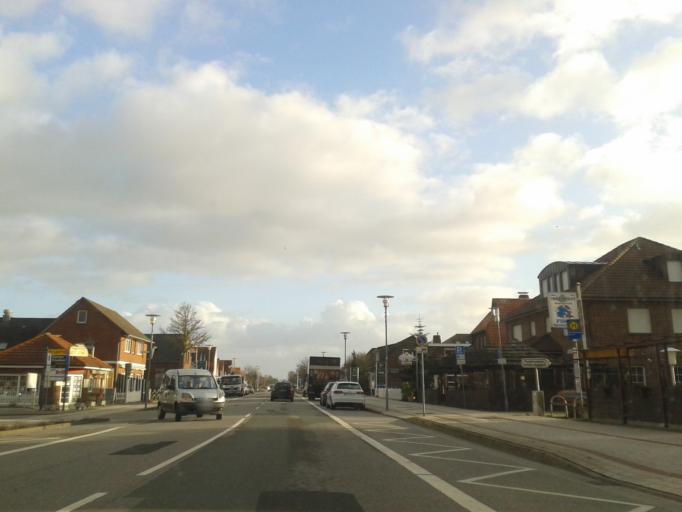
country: DE
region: Lower Saxony
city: Norddeich
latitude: 53.6185
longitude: 7.1593
